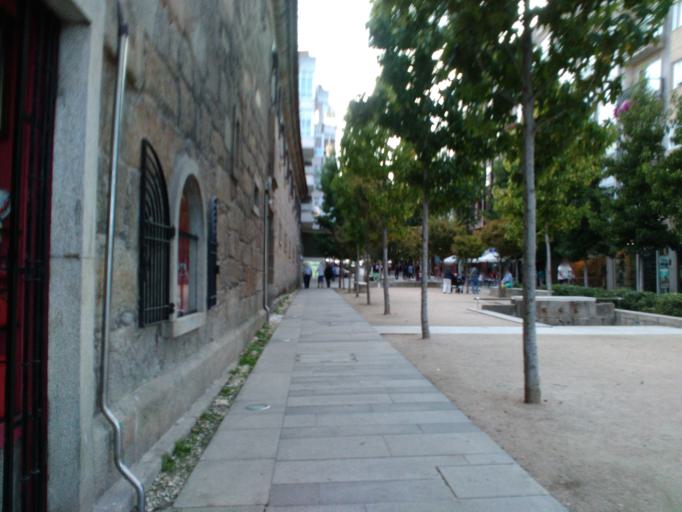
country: ES
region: Galicia
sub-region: Provincia de Pontevedra
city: Baiona
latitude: 42.1204
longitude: -8.8498
